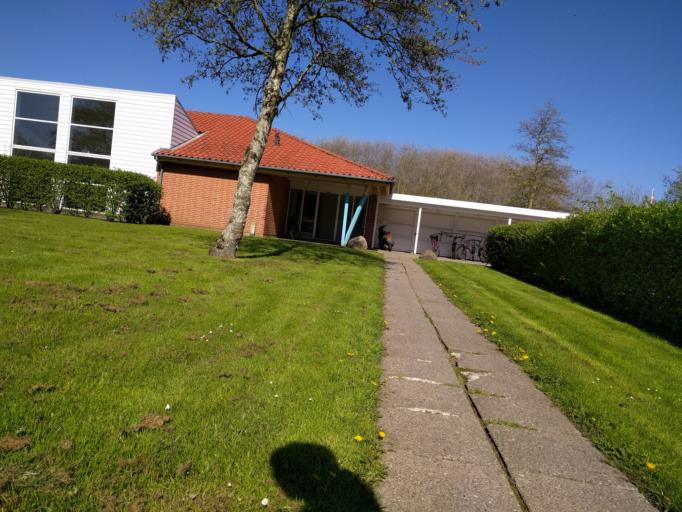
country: DK
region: Central Jutland
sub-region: Ringkobing-Skjern Kommune
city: Ringkobing
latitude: 56.0908
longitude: 8.2556
